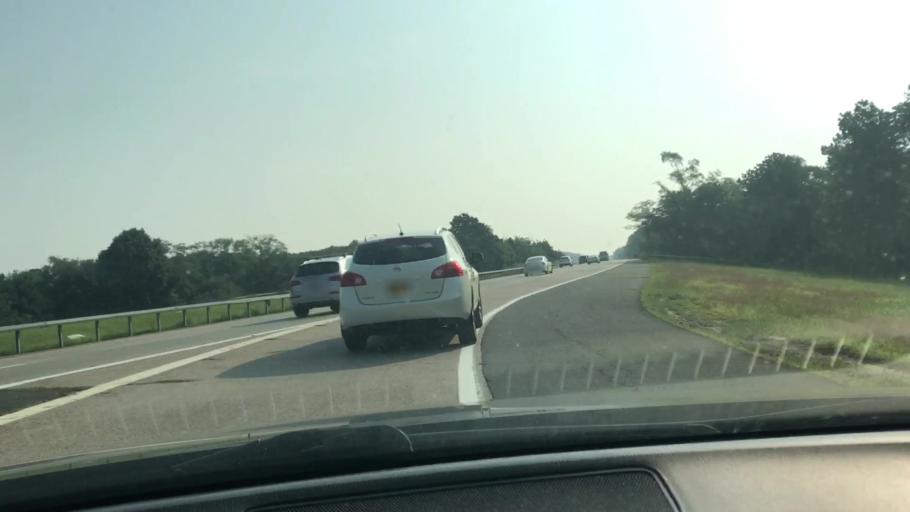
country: US
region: New York
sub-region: Suffolk County
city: Flanders
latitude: 40.8699
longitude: -72.6185
